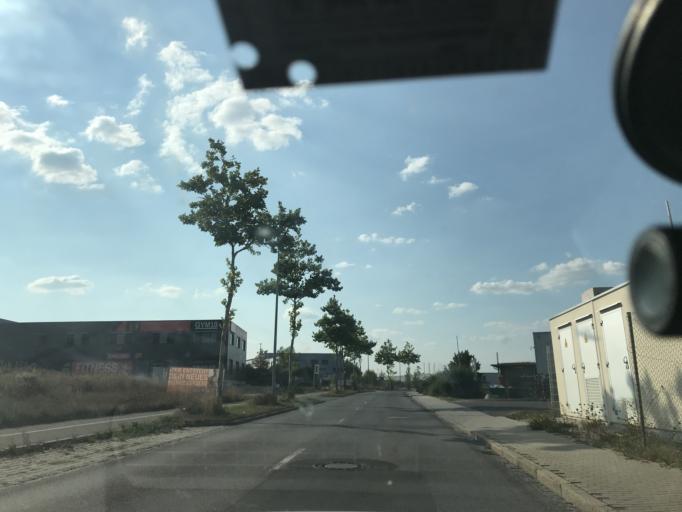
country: DE
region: Bavaria
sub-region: Upper Palatinate
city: Amberg
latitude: 49.4447
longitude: 11.8280
